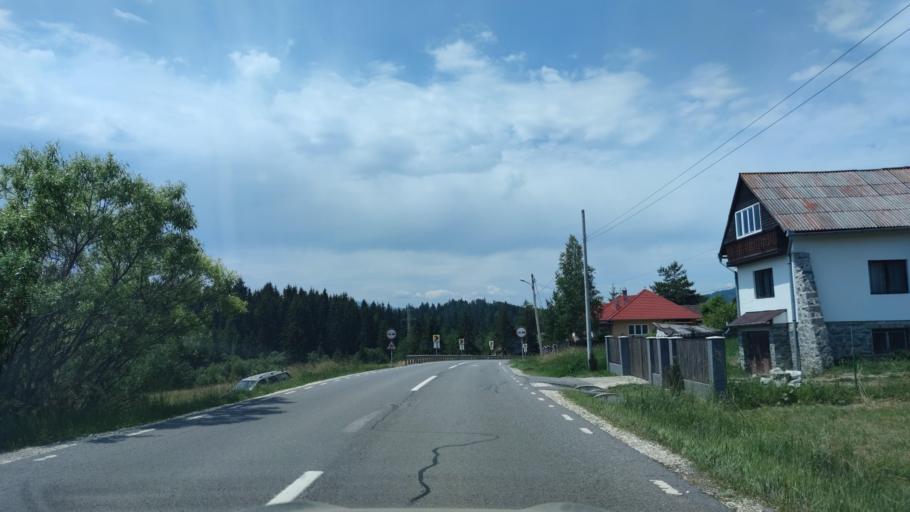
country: RO
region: Harghita
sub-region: Comuna Voslobeni
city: Voslobeni
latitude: 46.6193
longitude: 25.6959
